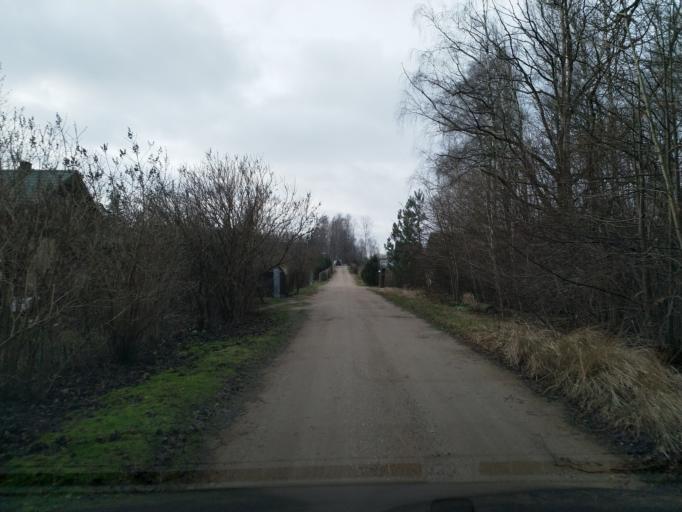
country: LV
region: Kuldigas Rajons
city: Kuldiga
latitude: 56.9491
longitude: 22.0059
